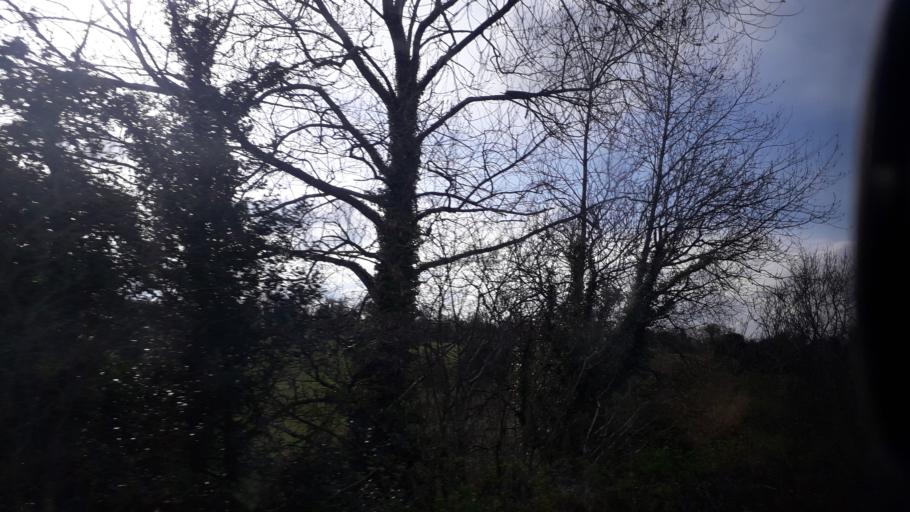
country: IE
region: Leinster
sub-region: An Mhi
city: Longwood
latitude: 53.4536
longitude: -6.9602
